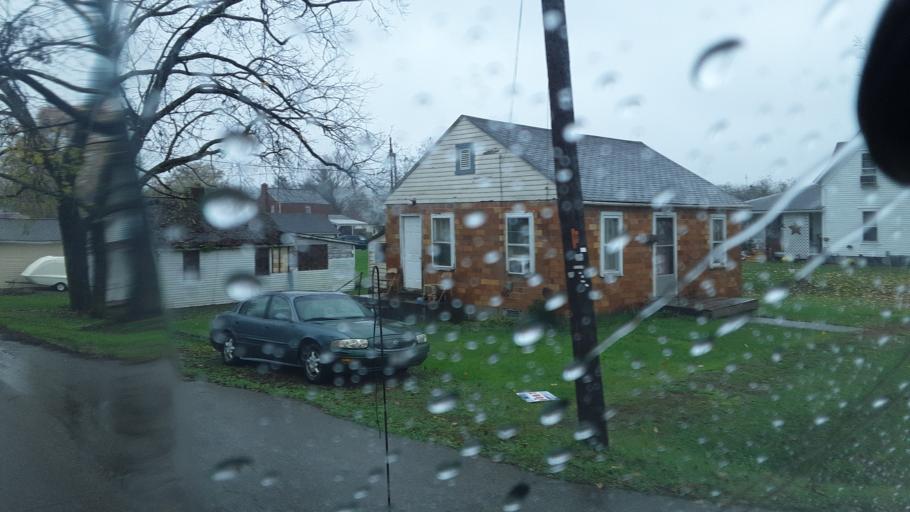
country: US
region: Ohio
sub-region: Vinton County
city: McArthur
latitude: 39.2481
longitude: -82.4833
